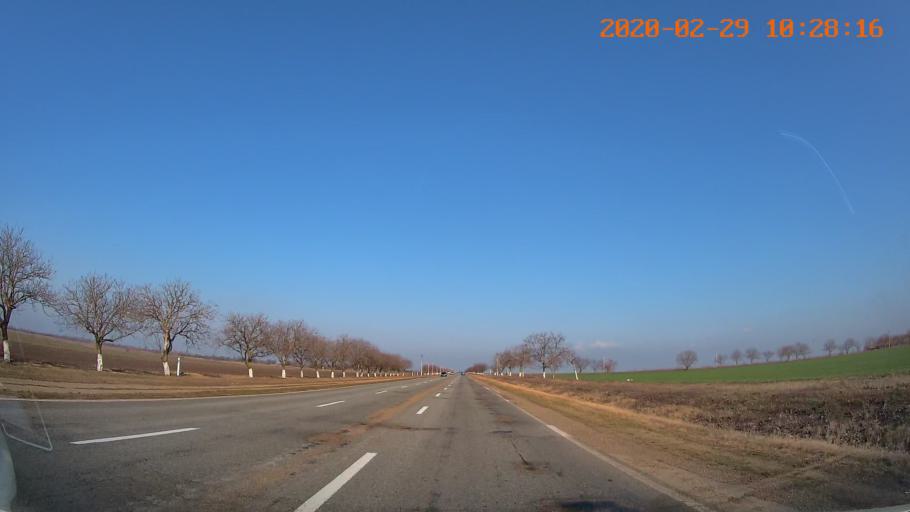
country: MD
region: Telenesti
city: Tiraspolul Nou
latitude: 46.9081
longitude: 29.5925
